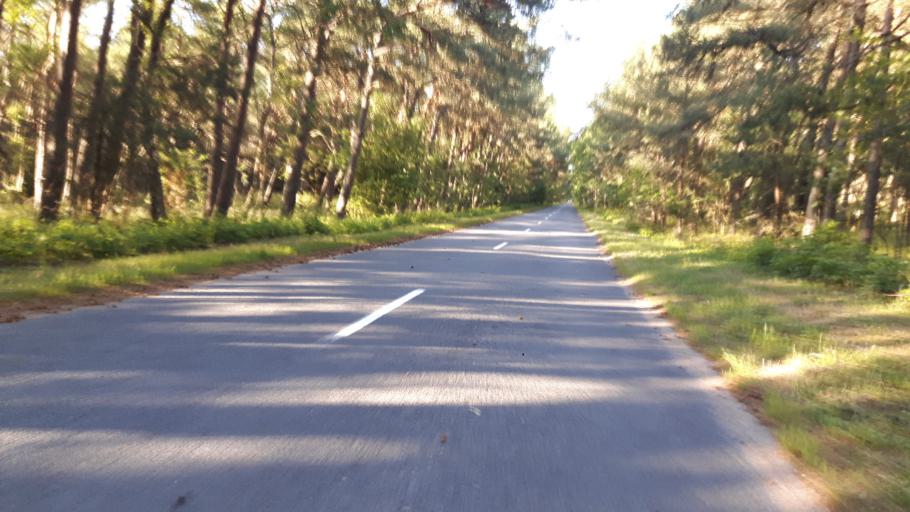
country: LT
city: Nida
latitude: 55.2453
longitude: 20.9201
